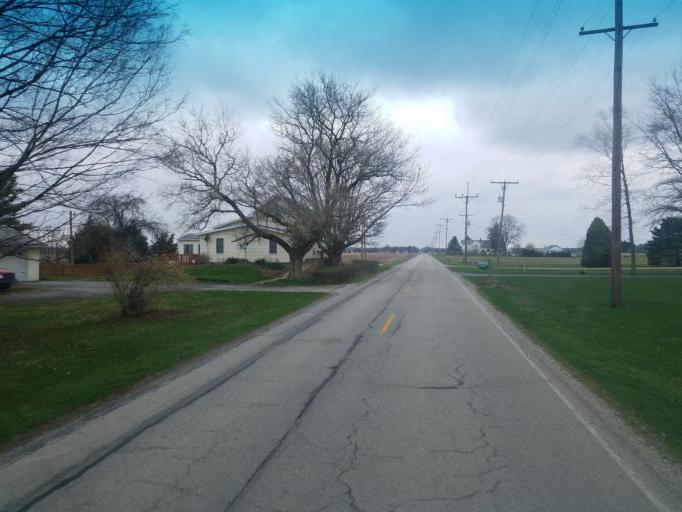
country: US
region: Ohio
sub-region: Marion County
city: Prospect
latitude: 40.5001
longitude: -83.1515
